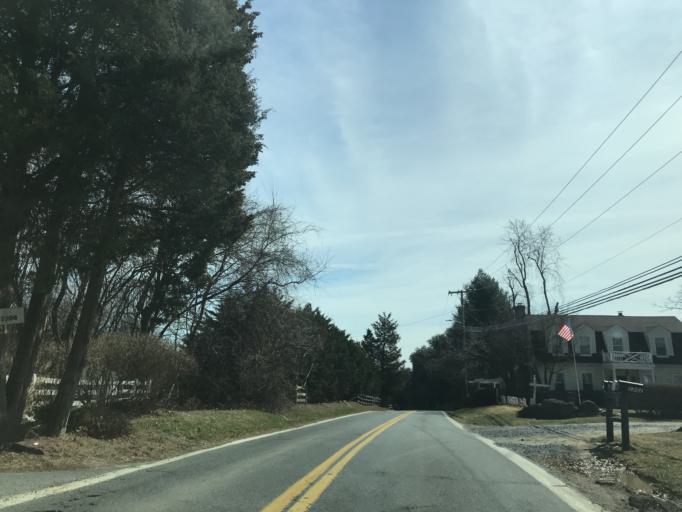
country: US
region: Maryland
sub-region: Montgomery County
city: Ashton-Sandy Spring
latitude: 39.1386
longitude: -76.9833
